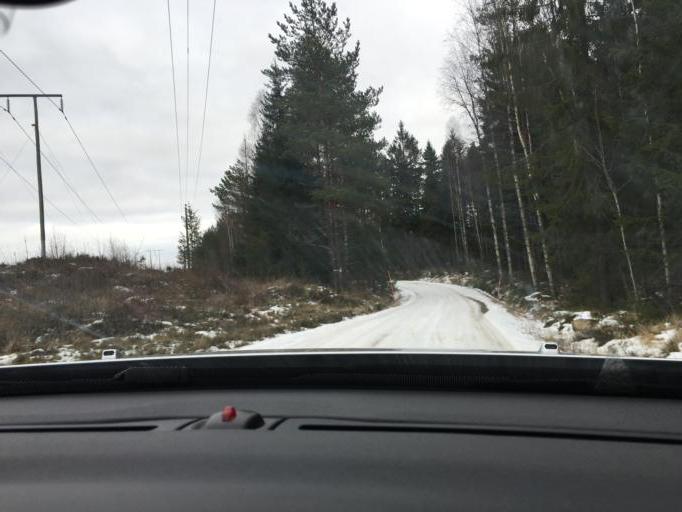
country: SE
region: Soedermanland
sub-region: Katrineholms Kommun
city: Katrineholm
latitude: 58.9966
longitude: 16.2750
